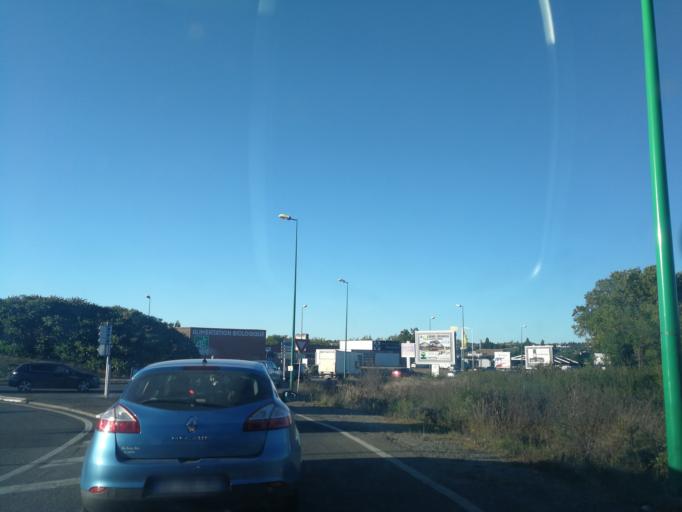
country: FR
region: Midi-Pyrenees
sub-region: Departement de la Haute-Garonne
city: Montrabe
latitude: 43.6380
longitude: 1.5013
